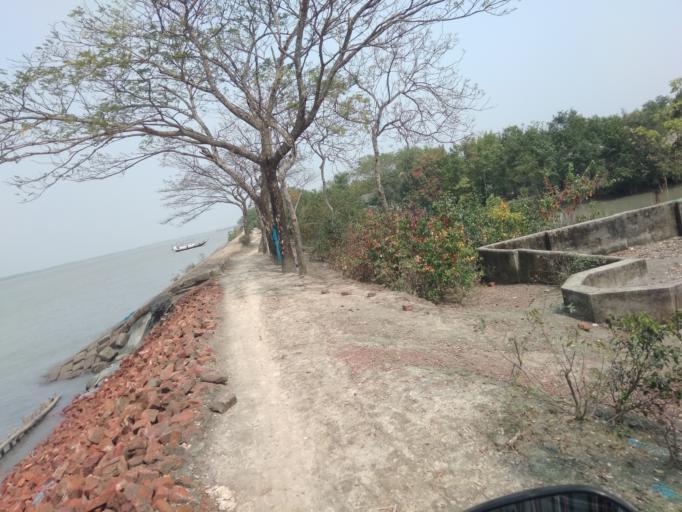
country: IN
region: West Bengal
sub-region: North 24 Parganas
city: Gosaba
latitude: 22.2514
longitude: 89.2503
